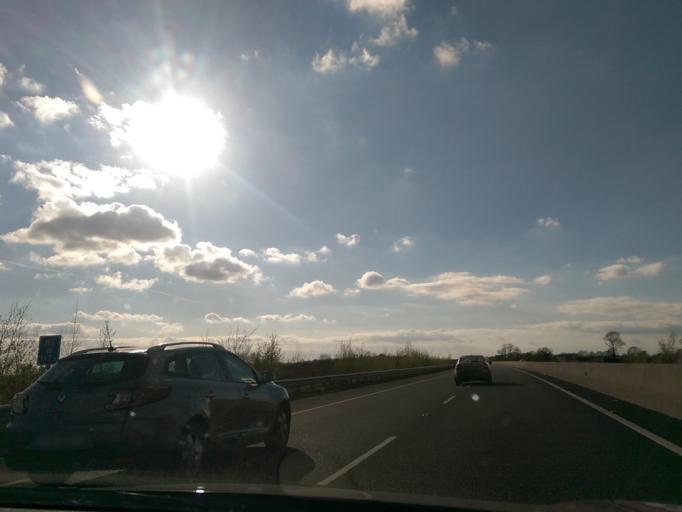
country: IE
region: Connaught
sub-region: County Galway
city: Loughrea
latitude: 53.2682
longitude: -8.6425
